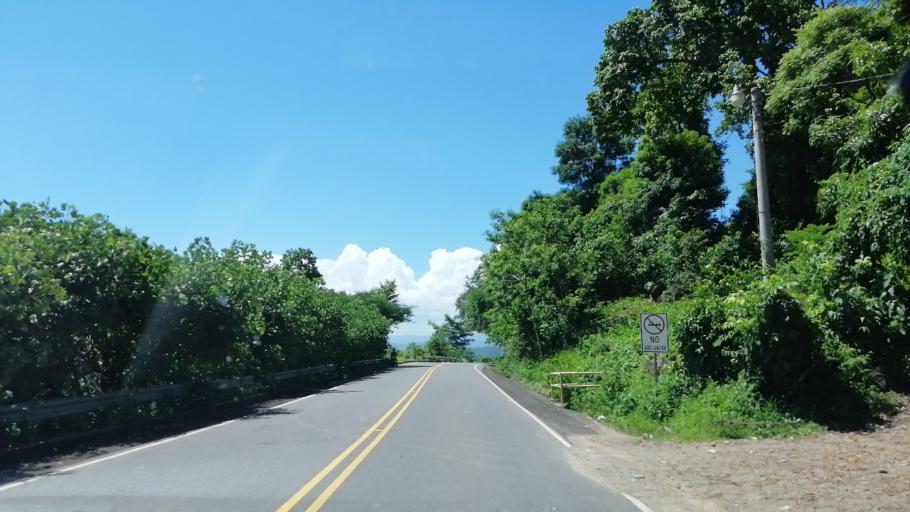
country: SV
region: San Miguel
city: Ciudad Barrios
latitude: 13.8064
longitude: -88.1912
